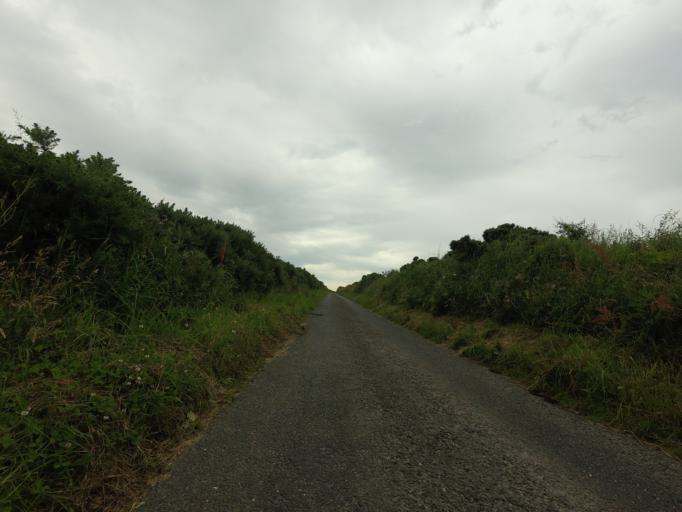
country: GB
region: Scotland
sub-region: Aberdeenshire
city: Whitehills
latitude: 57.6718
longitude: -2.5983
